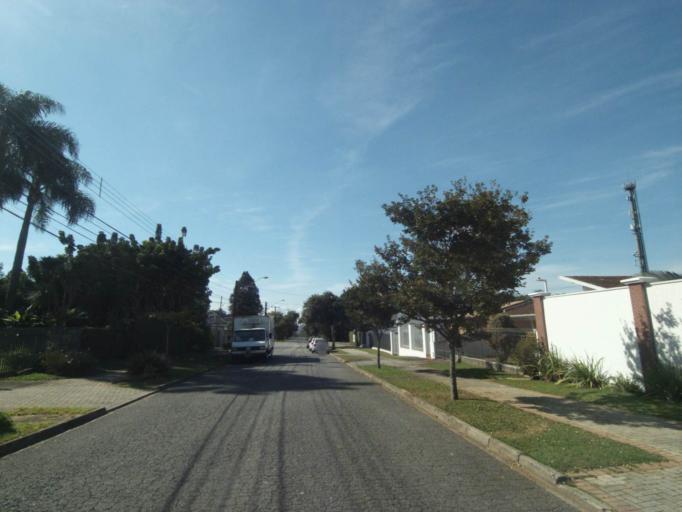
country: BR
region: Parana
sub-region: Curitiba
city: Curitiba
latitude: -25.4384
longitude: -49.2970
